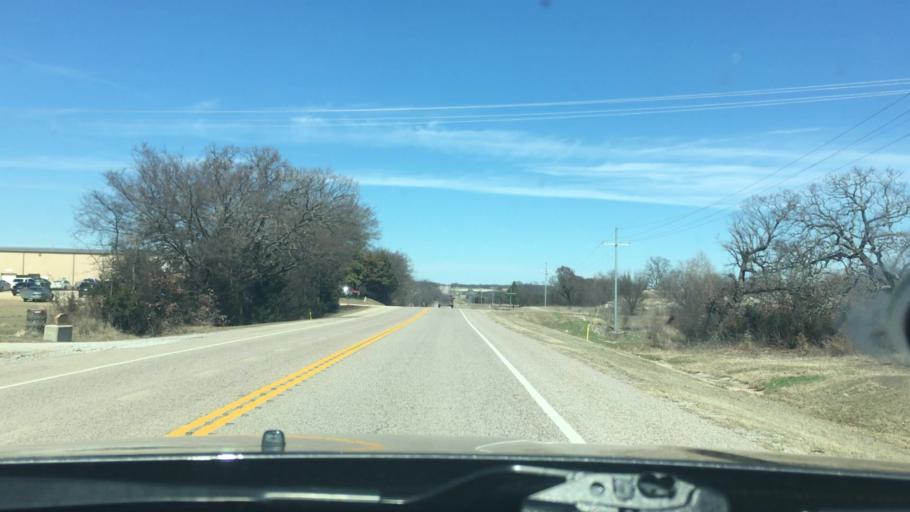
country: US
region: Oklahoma
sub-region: Murray County
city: Sulphur
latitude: 34.4192
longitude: -96.9508
